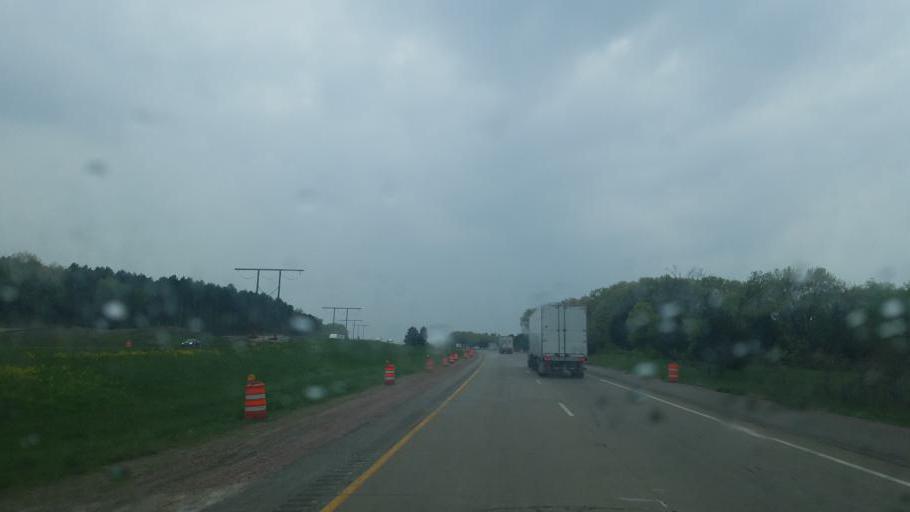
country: US
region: Wisconsin
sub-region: Sauk County
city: Baraboo
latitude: 43.5457
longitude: -89.6281
